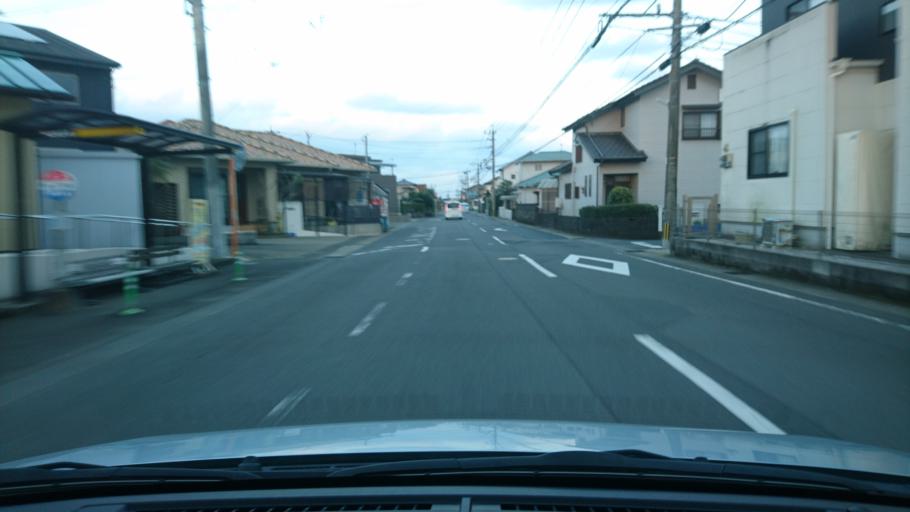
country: JP
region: Miyazaki
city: Miyazaki-shi
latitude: 31.8578
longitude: 131.4242
